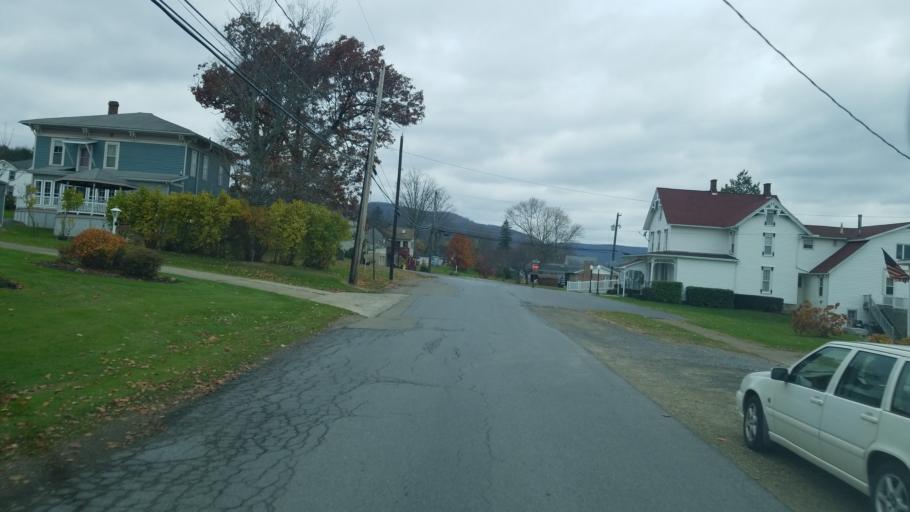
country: US
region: Pennsylvania
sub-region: McKean County
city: Smethport
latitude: 41.8061
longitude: -78.4406
